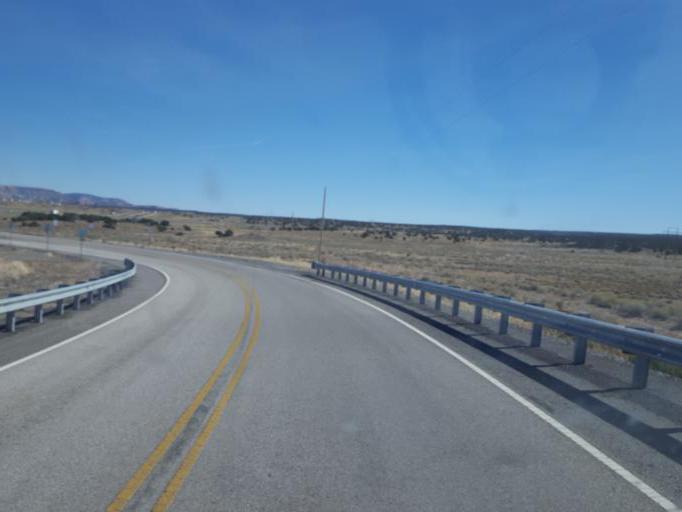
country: US
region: New Mexico
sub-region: McKinley County
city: Church Rock
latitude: 35.5004
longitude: -108.5056
